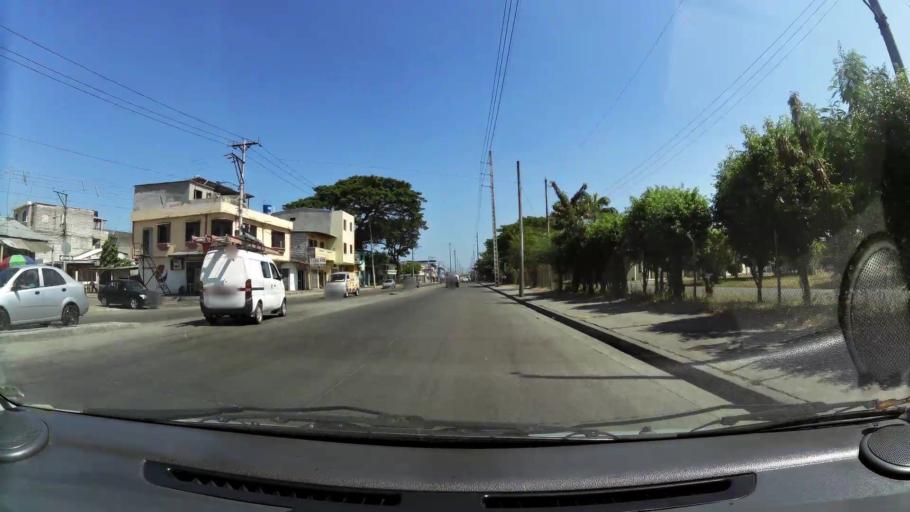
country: EC
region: Guayas
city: Guayaquil
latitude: -2.2203
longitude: -79.9394
